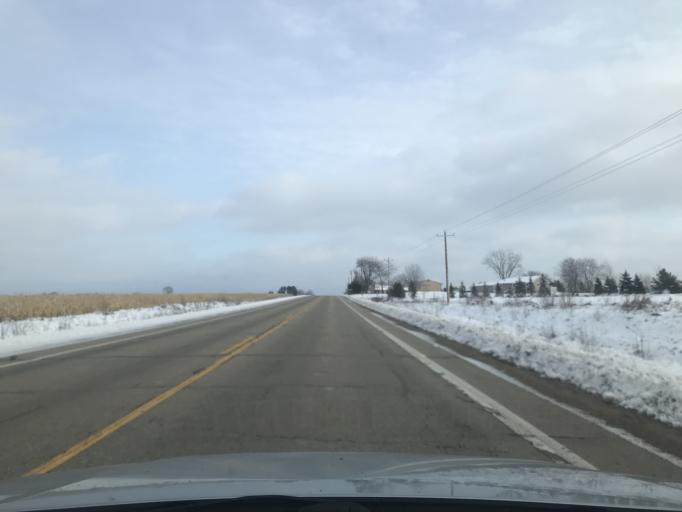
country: US
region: Wisconsin
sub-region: Oconto County
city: Oconto
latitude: 44.8929
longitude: -87.9734
